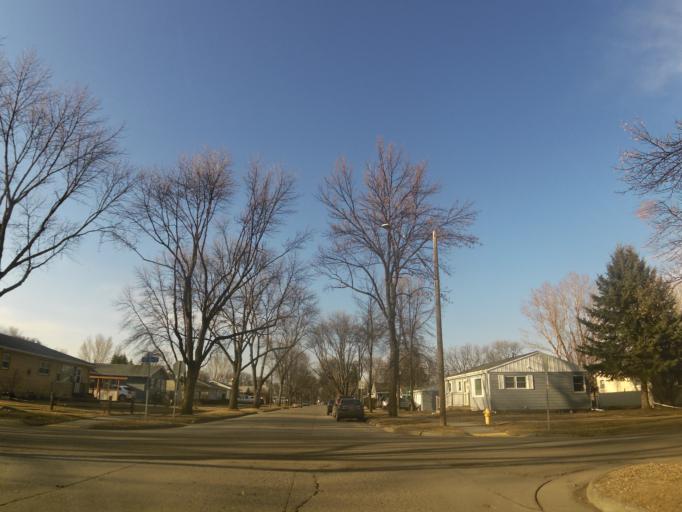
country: US
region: North Dakota
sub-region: Grand Forks County
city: Grand Forks
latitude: 47.9090
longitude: -97.0511
